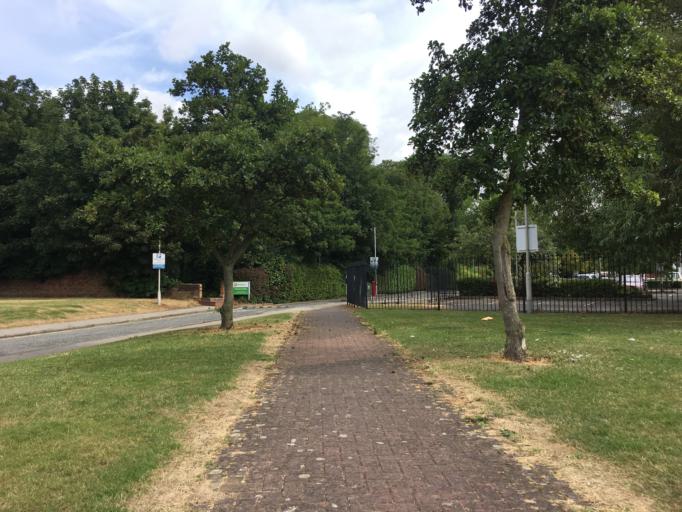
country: GB
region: England
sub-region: City of Kingston upon Hull
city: Hull
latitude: 53.7395
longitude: -0.3429
